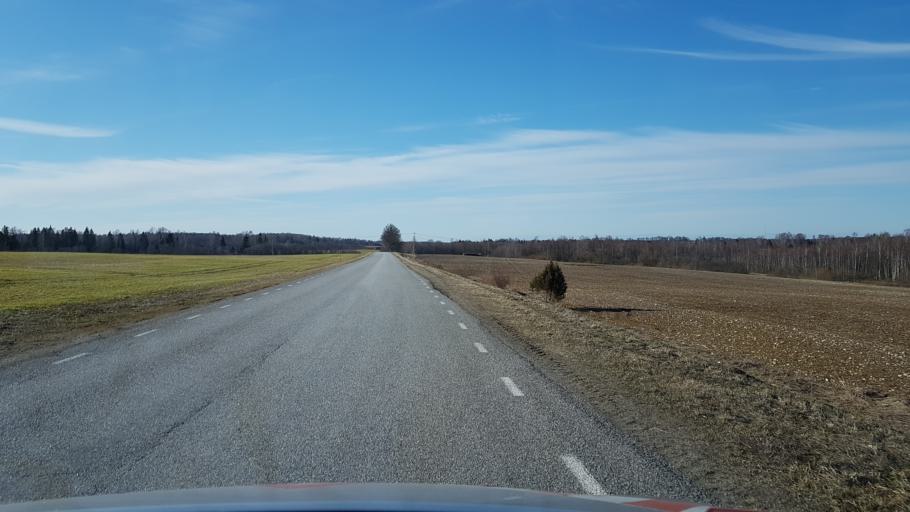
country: EE
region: Laeaene-Virumaa
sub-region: Kadrina vald
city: Kadrina
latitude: 59.2934
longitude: 26.1730
